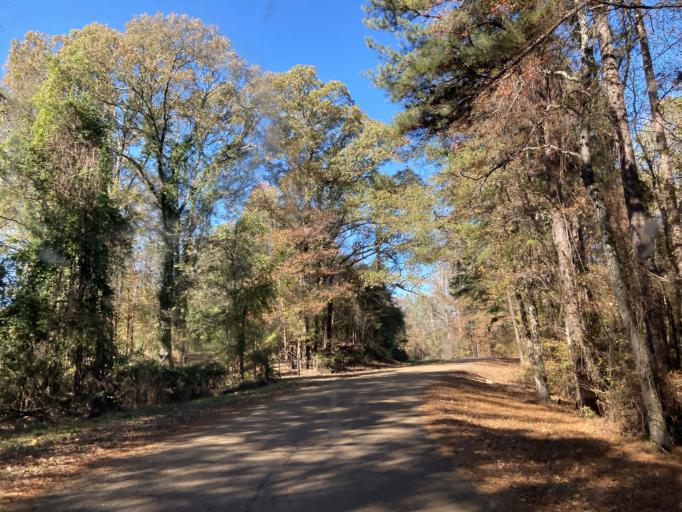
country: US
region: Mississippi
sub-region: Hinds County
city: Lynchburg
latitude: 32.5953
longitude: -90.5363
